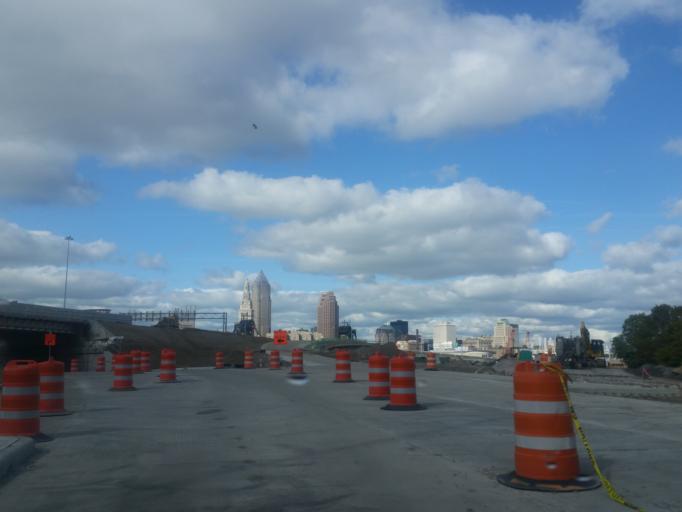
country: US
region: Ohio
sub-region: Cuyahoga County
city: Cleveland
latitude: 41.4823
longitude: -81.6914
